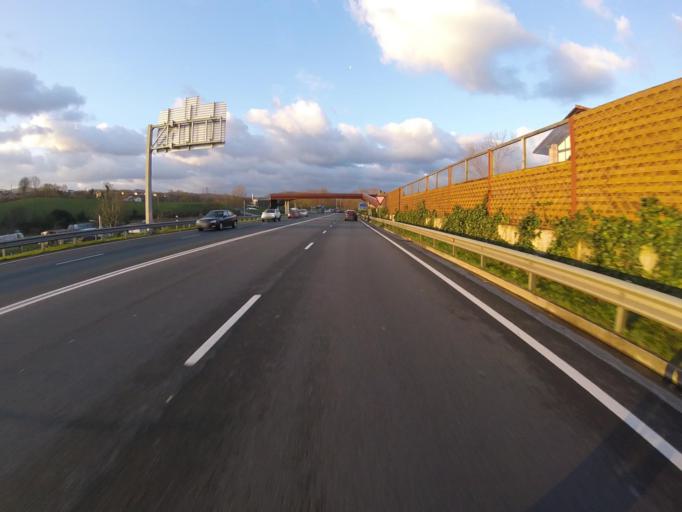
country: ES
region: Basque Country
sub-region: Provincia de Guipuzcoa
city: Irun
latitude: 43.3449
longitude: -1.8157
